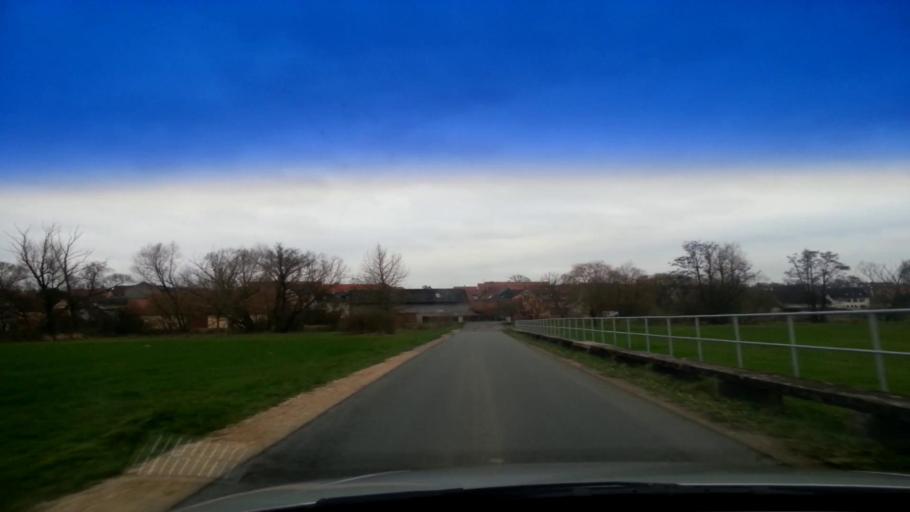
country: DE
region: Bavaria
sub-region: Upper Franconia
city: Walsdorf
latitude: 49.8209
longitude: 10.8075
